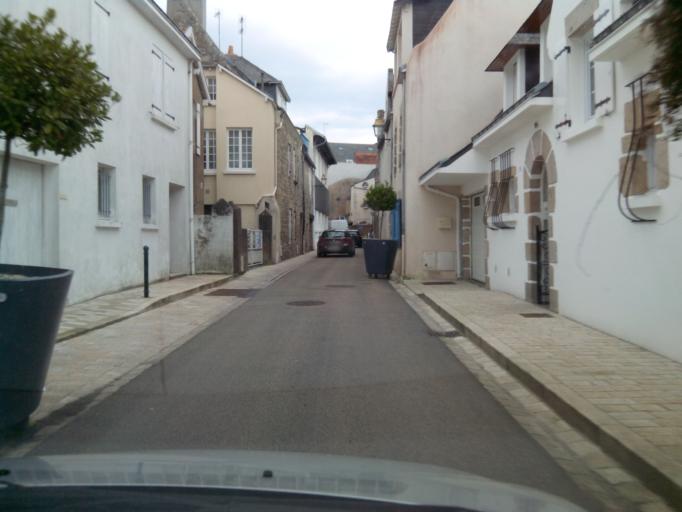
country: FR
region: Pays de la Loire
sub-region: Departement de la Loire-Atlantique
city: Le Pouliguen
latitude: 47.2781
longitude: -2.4297
